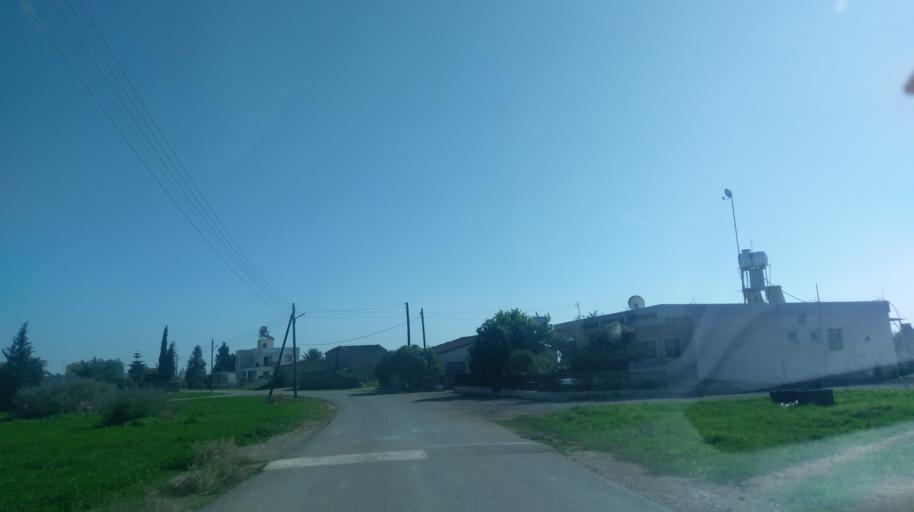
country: CY
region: Ammochostos
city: Trikomo
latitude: 35.2391
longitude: 33.8539
